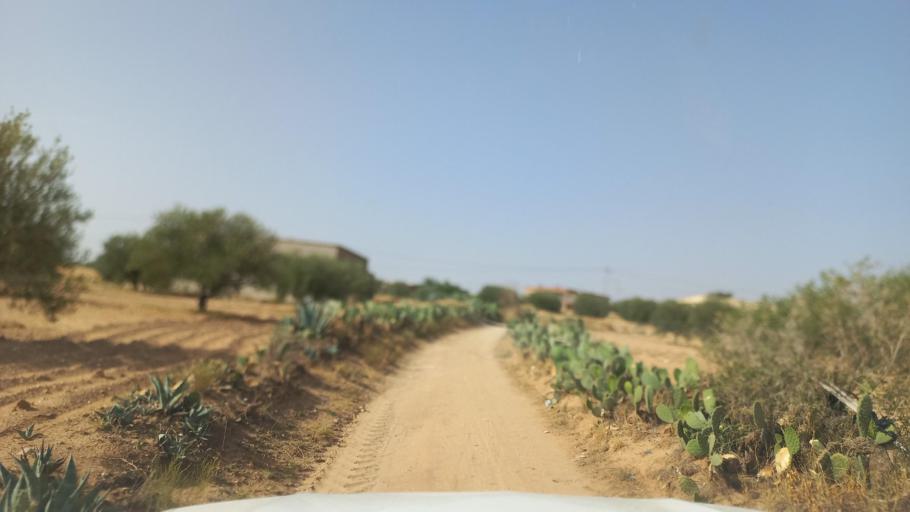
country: TN
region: Al Qasrayn
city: Kasserine
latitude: 35.2978
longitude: 8.9571
